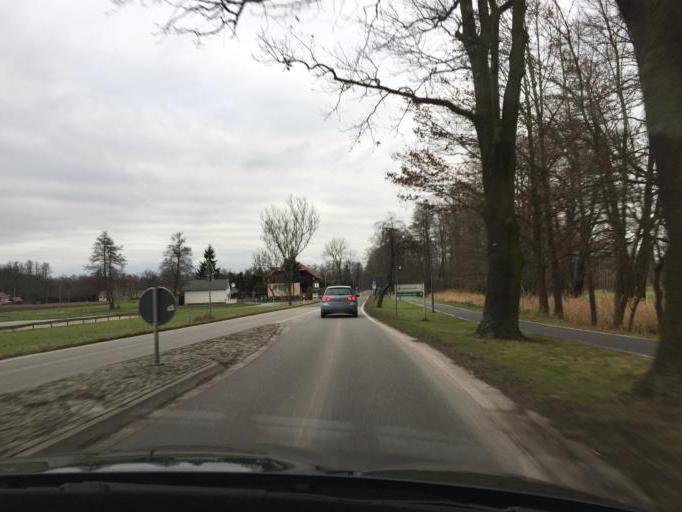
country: DE
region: Brandenburg
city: Burg
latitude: 51.8382
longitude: 14.1493
